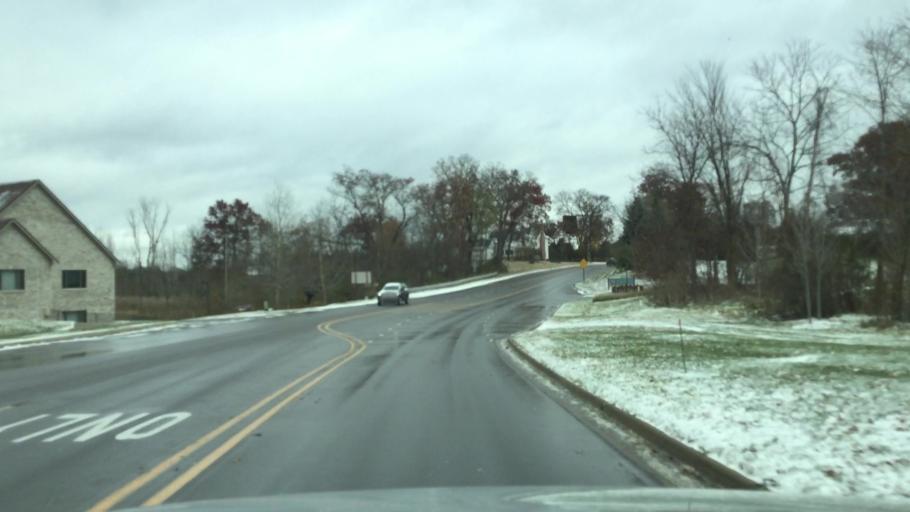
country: US
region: Michigan
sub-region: Livingston County
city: Brighton
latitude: 42.5369
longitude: -83.7534
